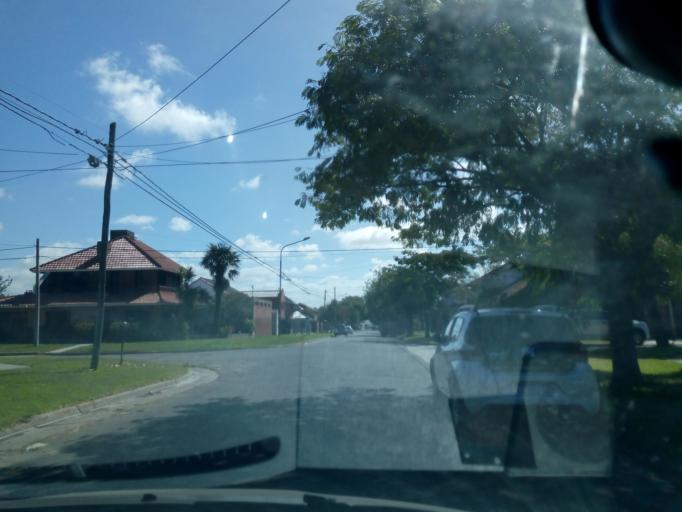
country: AR
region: Buenos Aires
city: Mar del Plata
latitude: -38.0538
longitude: -57.5544
